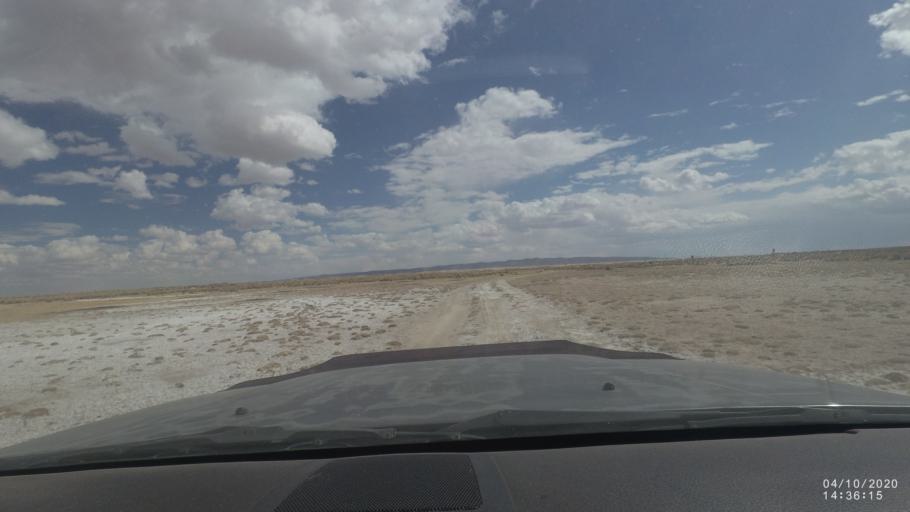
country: BO
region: Oruro
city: Poopo
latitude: -18.6724
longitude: -67.4698
